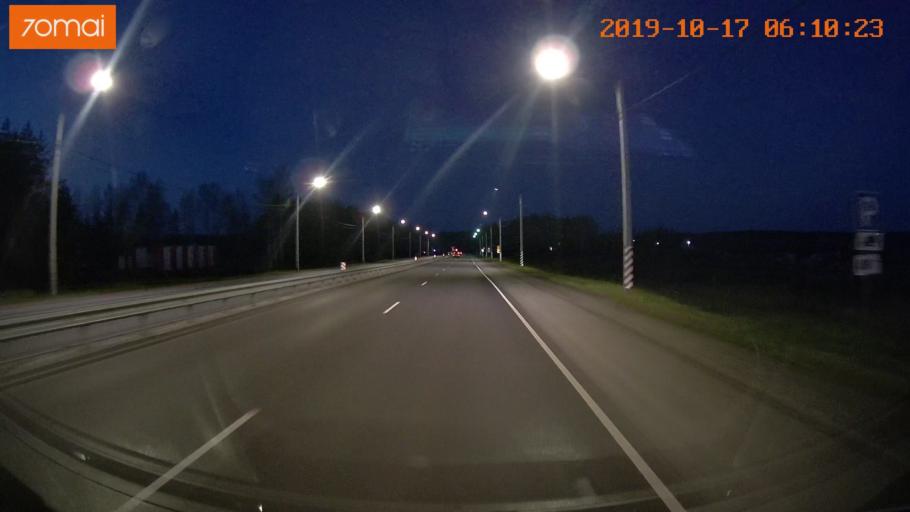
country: RU
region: Ivanovo
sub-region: Gorod Ivanovo
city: Ivanovo
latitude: 56.9321
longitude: 40.9660
